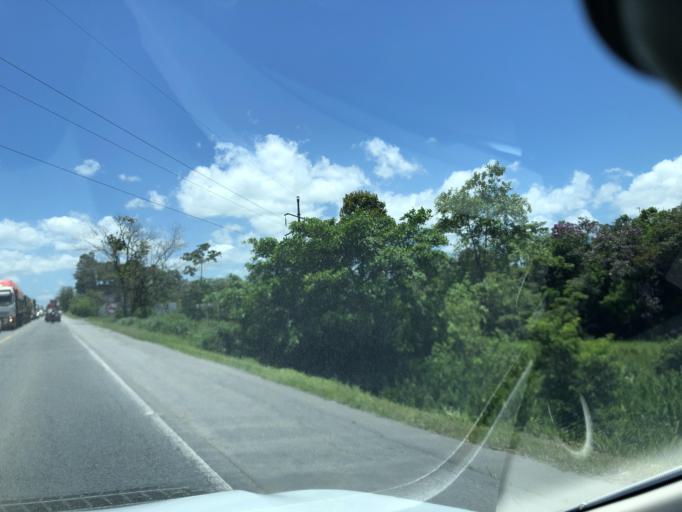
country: BR
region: Santa Catarina
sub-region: Joinville
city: Joinville
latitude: -26.4161
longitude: -48.7702
